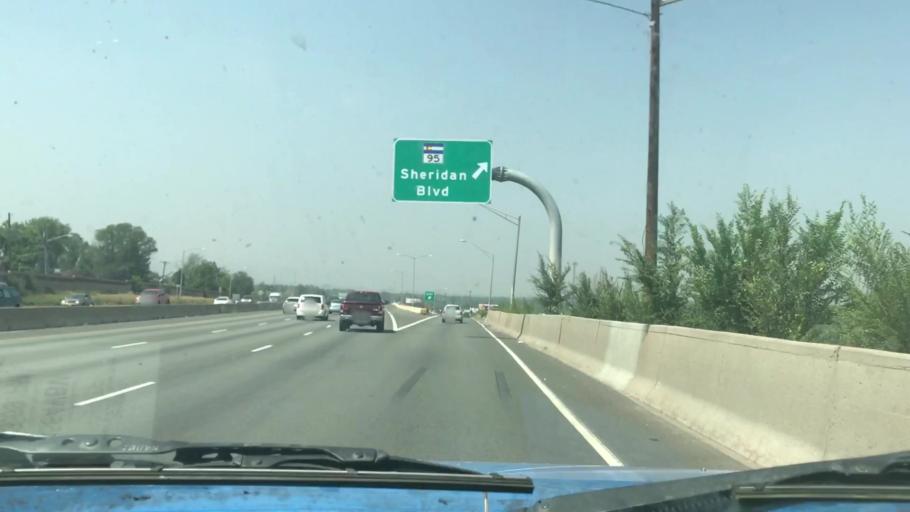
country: US
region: Colorado
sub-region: Jefferson County
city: Edgewater
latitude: 39.7260
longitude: -105.0487
